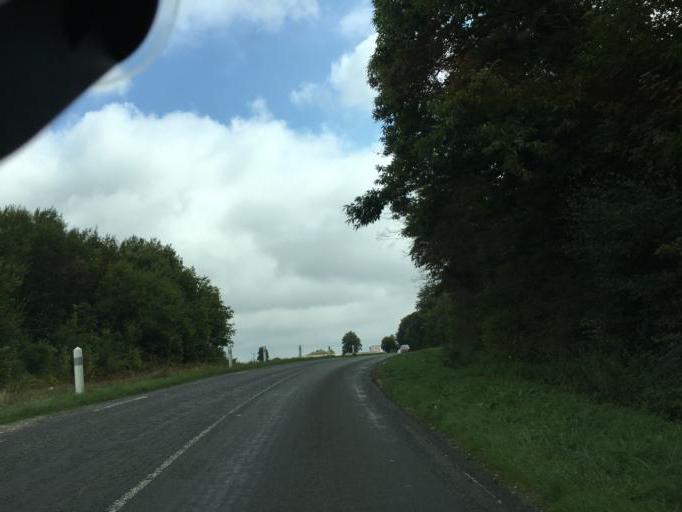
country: FR
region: Nord-Pas-de-Calais
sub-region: Departement du Pas-de-Calais
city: Rang-du-Fliers
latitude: 50.4194
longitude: 1.6649
